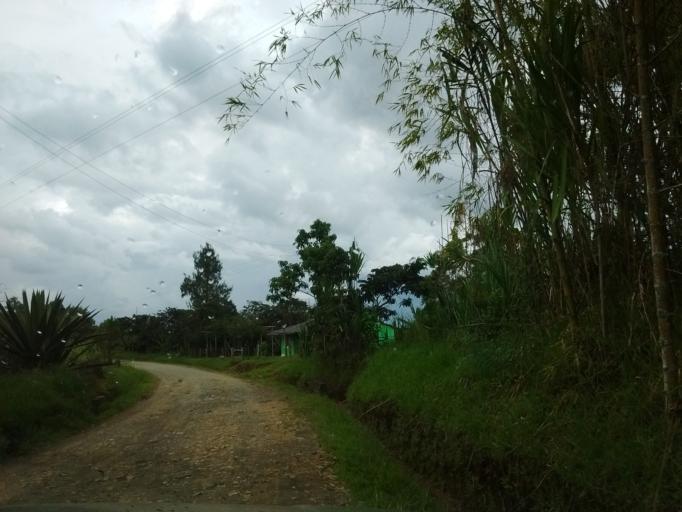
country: CO
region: Cauca
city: Cajibio
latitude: 2.5840
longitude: -76.6726
